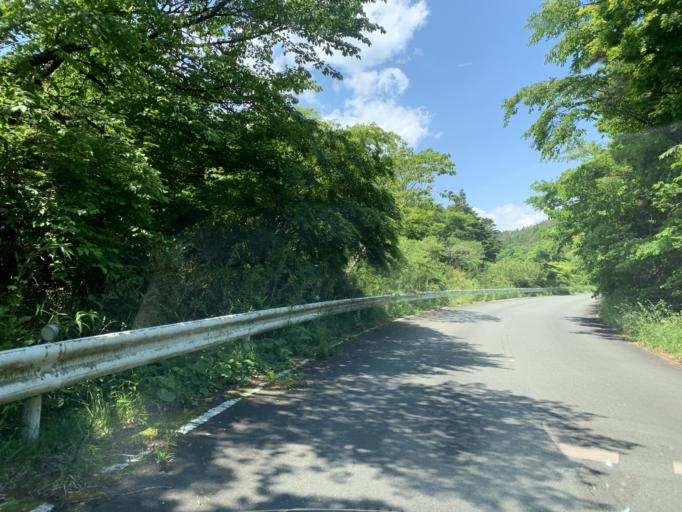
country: JP
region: Miyagi
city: Matsushima
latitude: 38.3538
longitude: 141.0576
